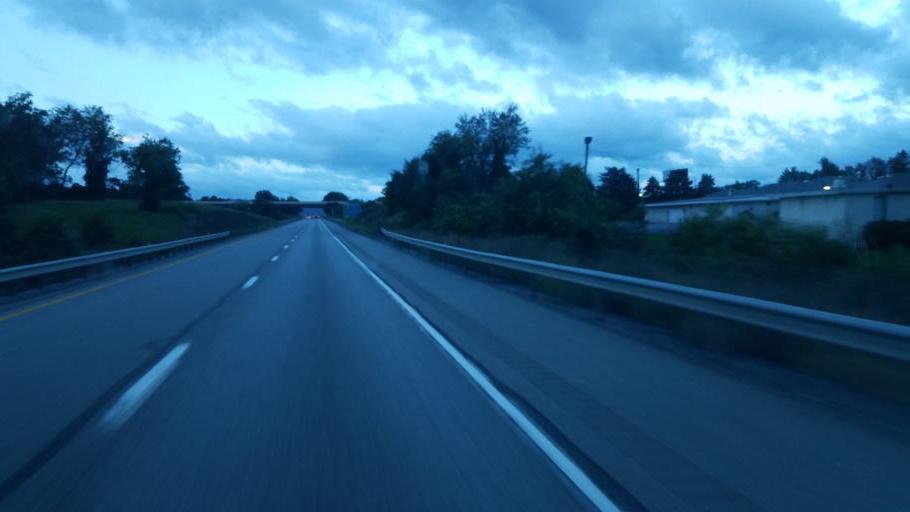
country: US
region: Pennsylvania
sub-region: Bedford County
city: Earlston
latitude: 39.9891
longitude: -78.2431
